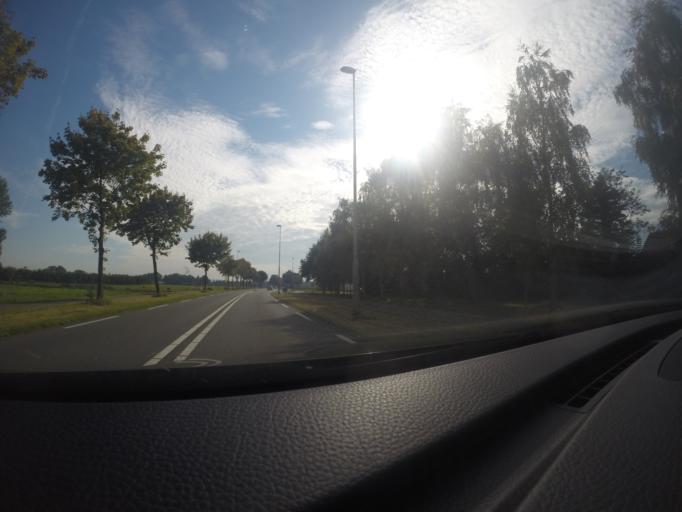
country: NL
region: Gelderland
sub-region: Gemeente Doetinchem
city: Doetinchem
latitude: 51.9602
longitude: 6.2200
